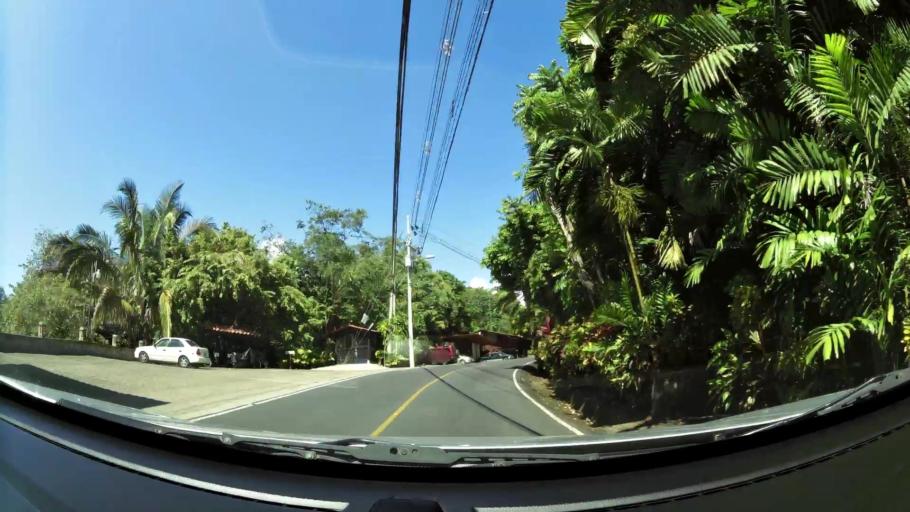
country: CR
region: Puntarenas
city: Quepos
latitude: 9.3993
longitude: -84.1541
